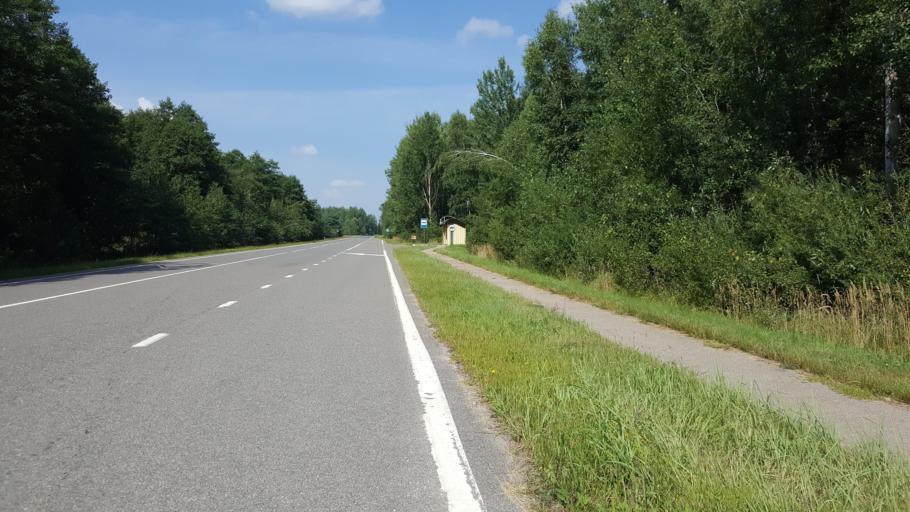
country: BY
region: Brest
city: Kamyanyuki
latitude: 52.5508
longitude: 23.6458
